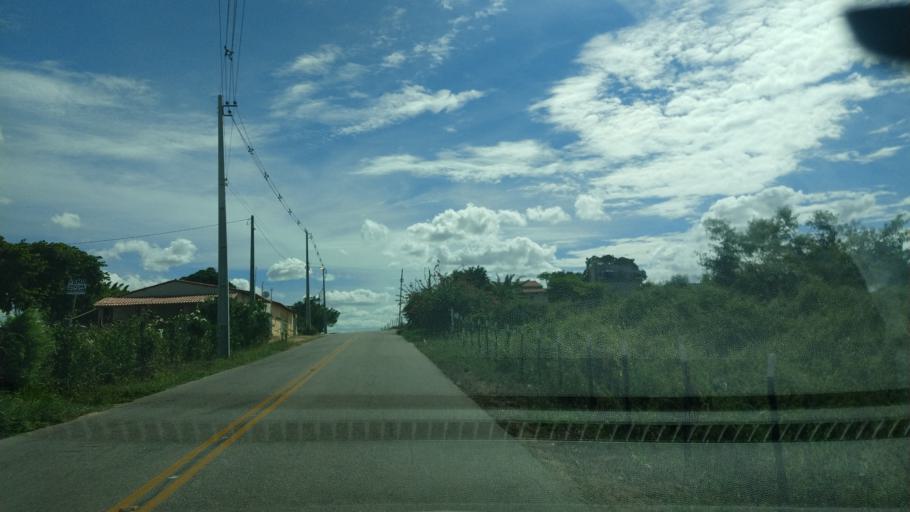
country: BR
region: Rio Grande do Norte
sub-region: Sao Jose Do Campestre
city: Sao Jose do Campestre
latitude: -6.4225
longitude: -35.7357
